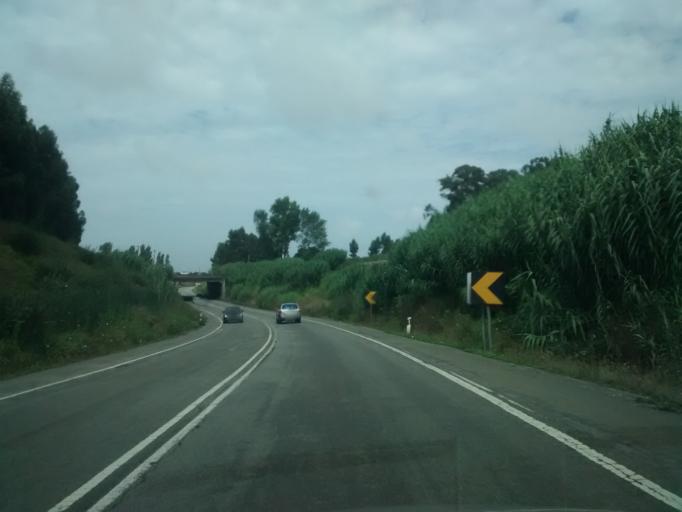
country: PT
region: Aveiro
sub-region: Aveiro
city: Aradas
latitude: 40.6105
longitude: -8.6264
